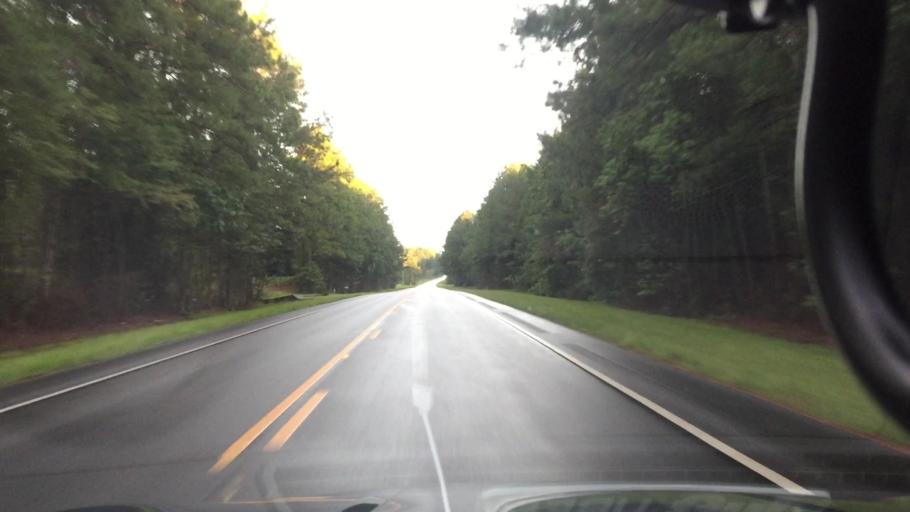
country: US
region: Alabama
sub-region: Coffee County
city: New Brockton
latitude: 31.5591
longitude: -85.9231
